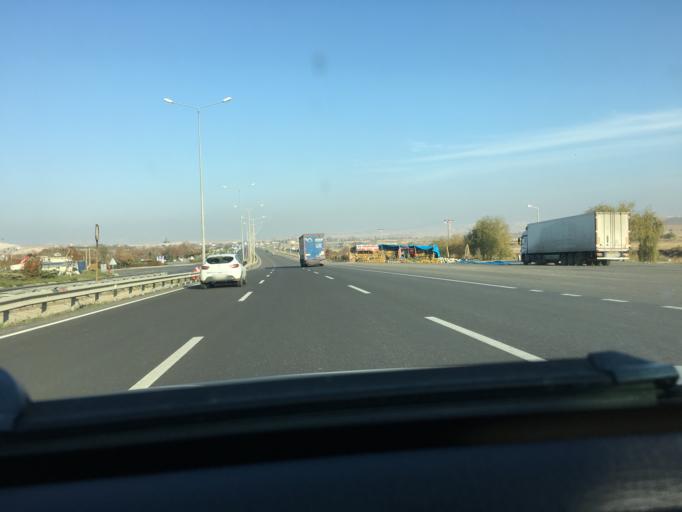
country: TR
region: Ankara
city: Temelli
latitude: 39.7252
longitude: 32.3575
